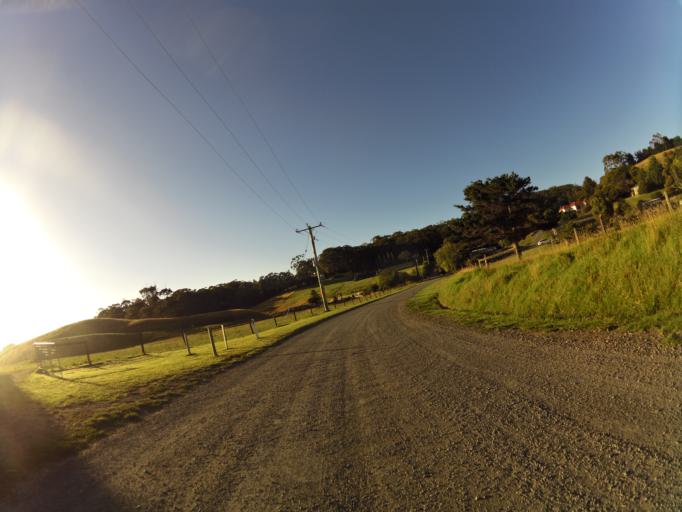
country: AU
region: Victoria
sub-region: Colac-Otway
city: Apollo Bay
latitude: -38.7698
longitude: 143.6465
